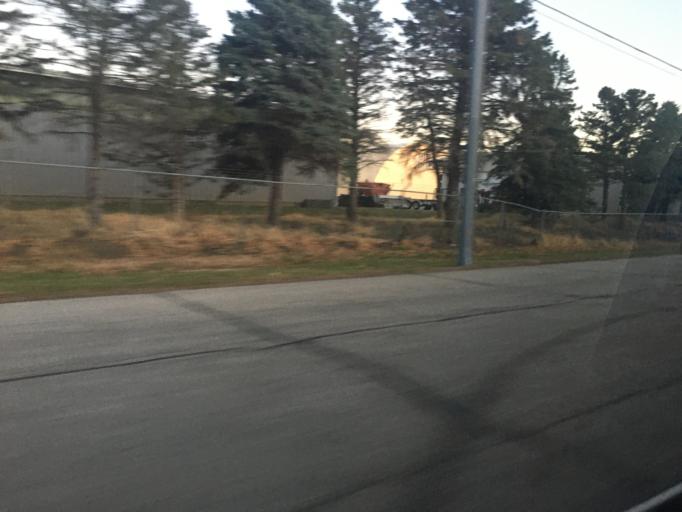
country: US
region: Minnesota
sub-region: Olmsted County
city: Rochester
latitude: 44.0708
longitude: -92.5088
